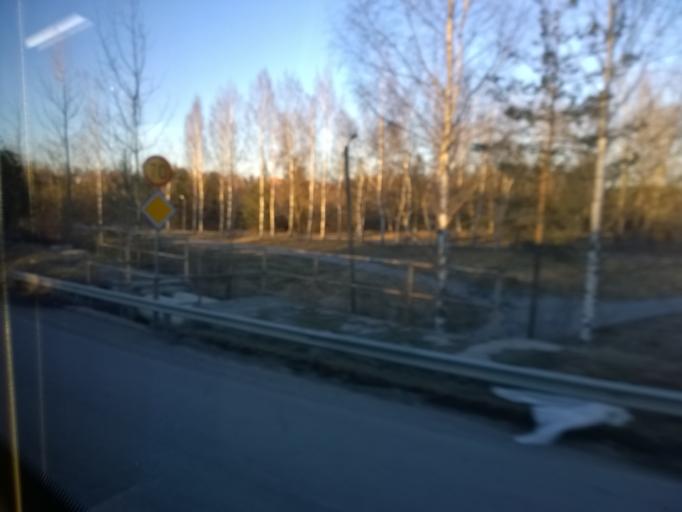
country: FI
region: Pirkanmaa
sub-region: Tampere
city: Tampere
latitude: 61.4813
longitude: 23.8297
